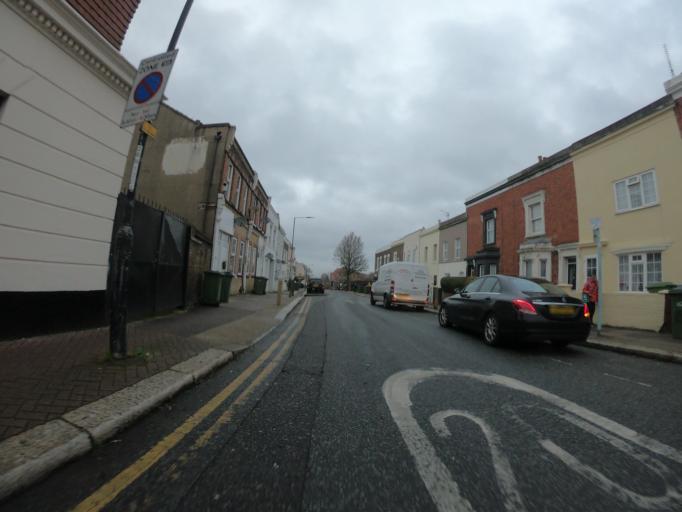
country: GB
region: England
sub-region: Greater London
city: Woolwich
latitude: 51.4823
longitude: 0.0698
